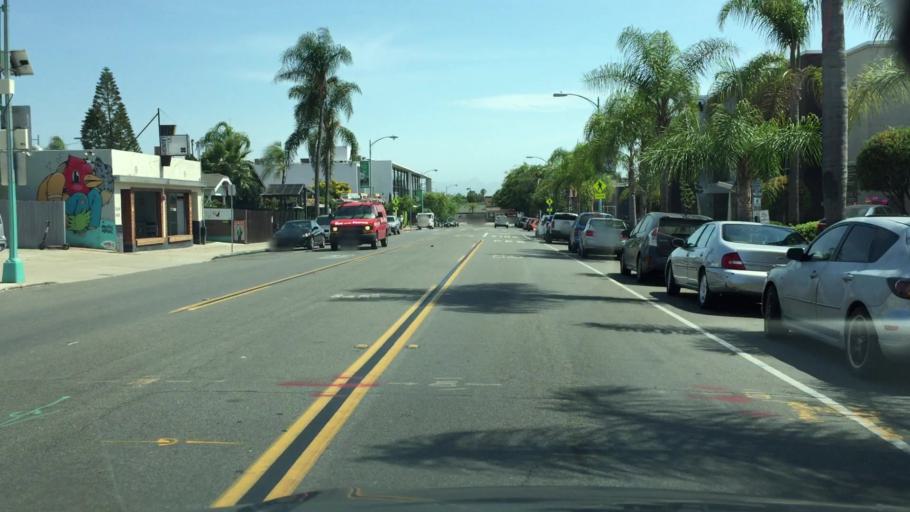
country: US
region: California
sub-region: San Diego County
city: San Diego
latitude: 32.7429
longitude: -117.1301
